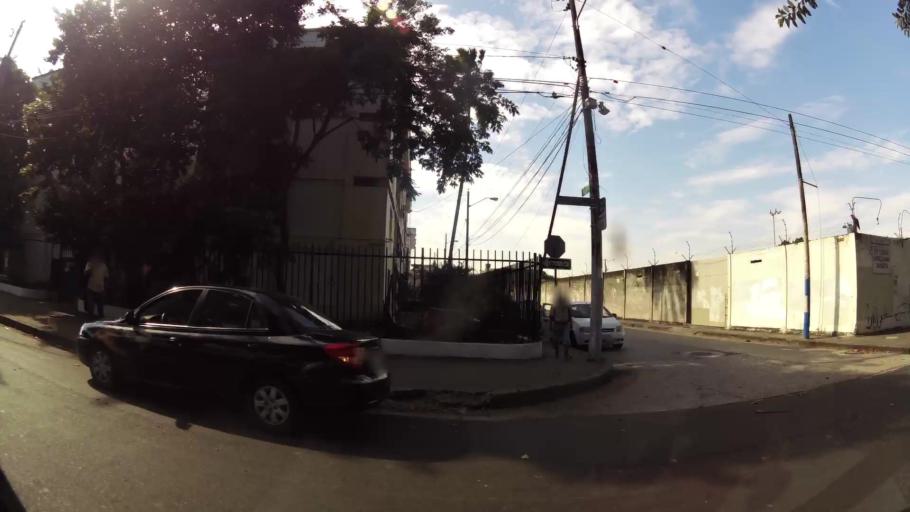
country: EC
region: Guayas
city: Guayaquil
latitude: -2.2231
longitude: -79.8967
